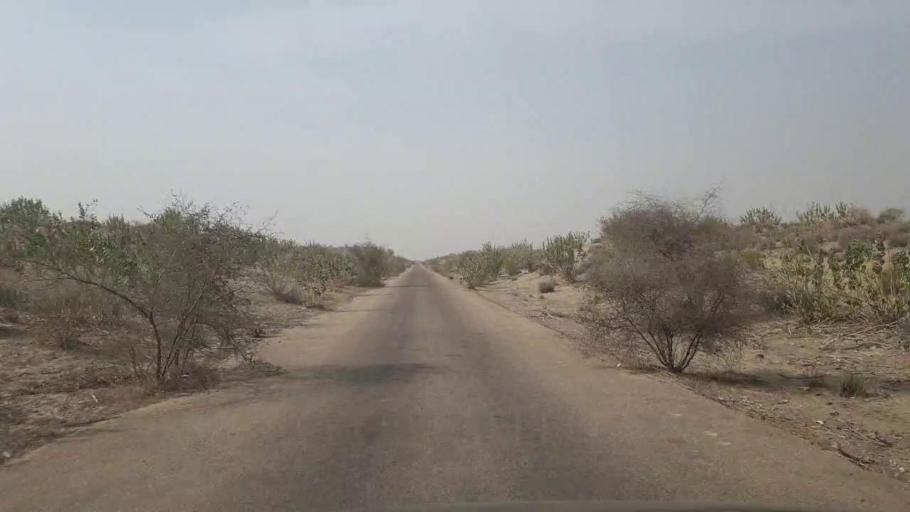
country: PK
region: Sindh
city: Chor
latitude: 25.6034
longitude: 69.9389
